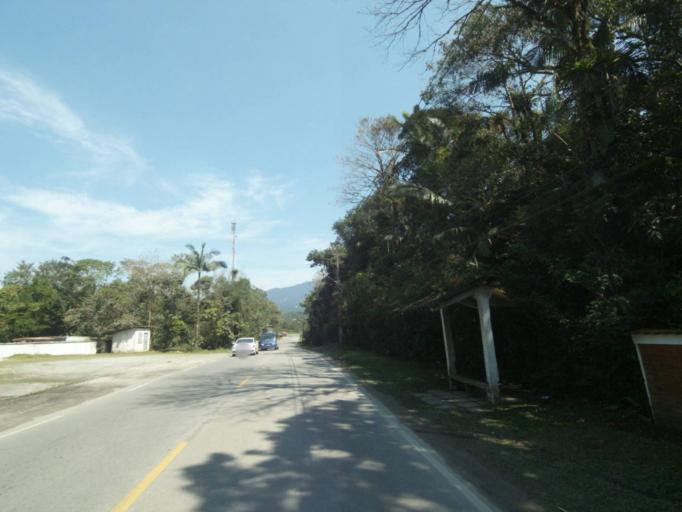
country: BR
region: Parana
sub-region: Paranagua
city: Paranagua
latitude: -25.5630
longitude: -48.6274
